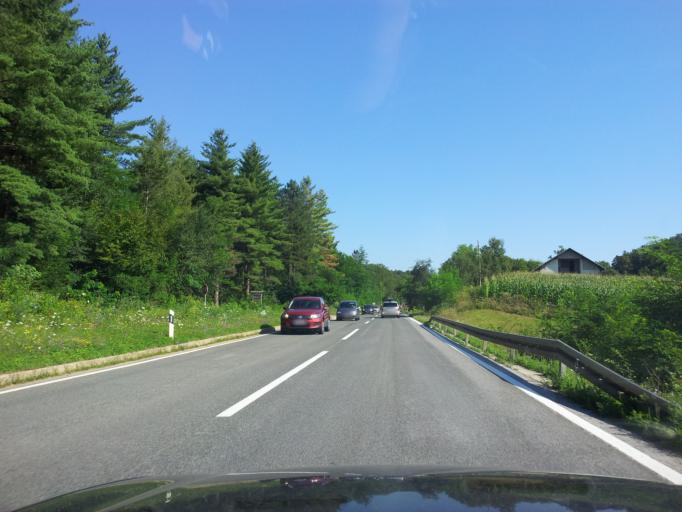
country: HR
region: Karlovacka
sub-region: Grad Karlovac
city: Slunj
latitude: 45.1782
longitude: 15.5604
